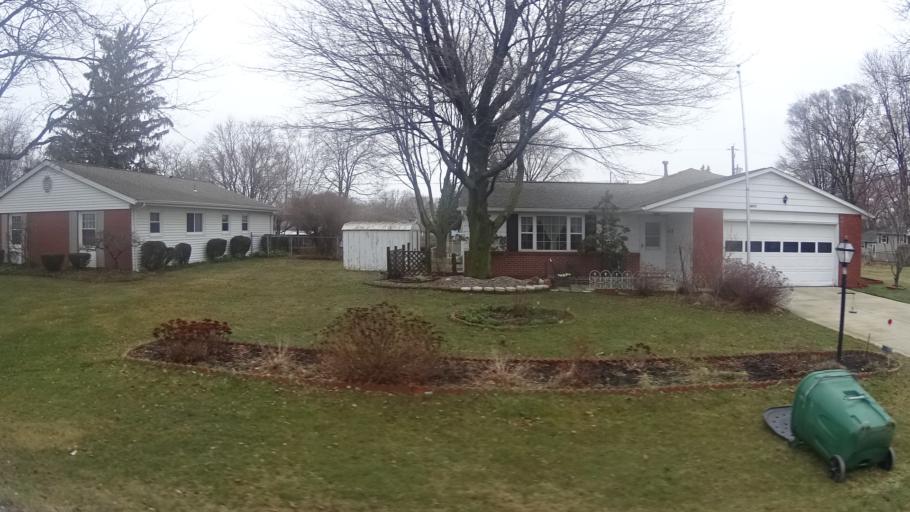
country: US
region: Ohio
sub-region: Erie County
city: Sandusky
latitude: 41.4234
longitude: -82.6549
